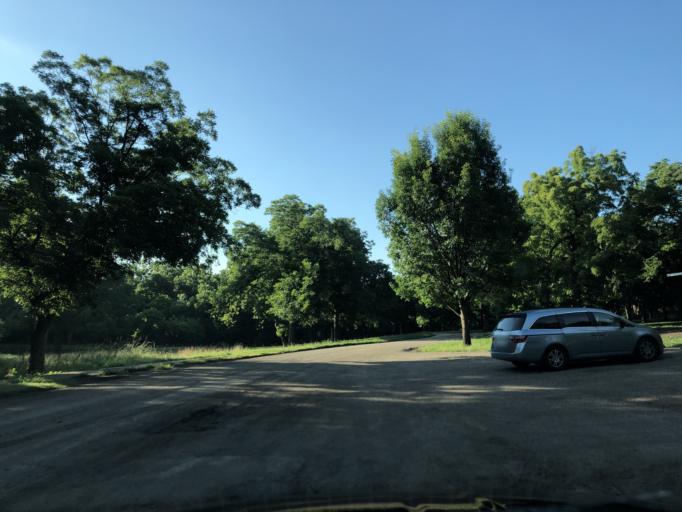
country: US
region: Texas
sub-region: Dallas County
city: Garland
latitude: 32.8490
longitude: -96.6138
